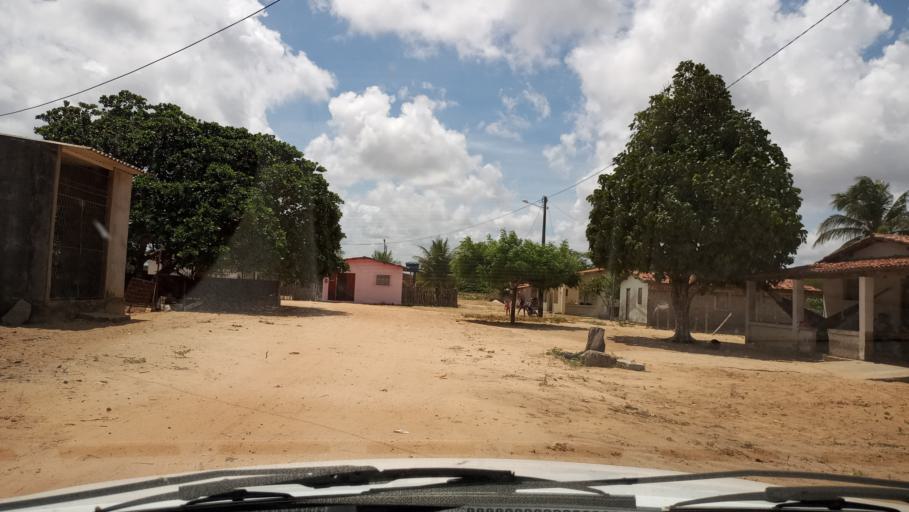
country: BR
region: Rio Grande do Norte
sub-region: Maxaranguape
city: Sao Miguel
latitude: -5.4804
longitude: -35.3300
